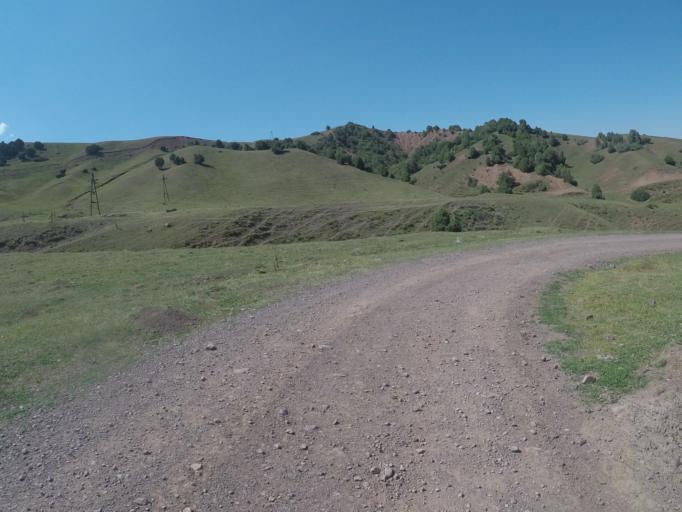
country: KG
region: Chuy
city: Bishkek
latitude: 42.6460
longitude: 74.5730
